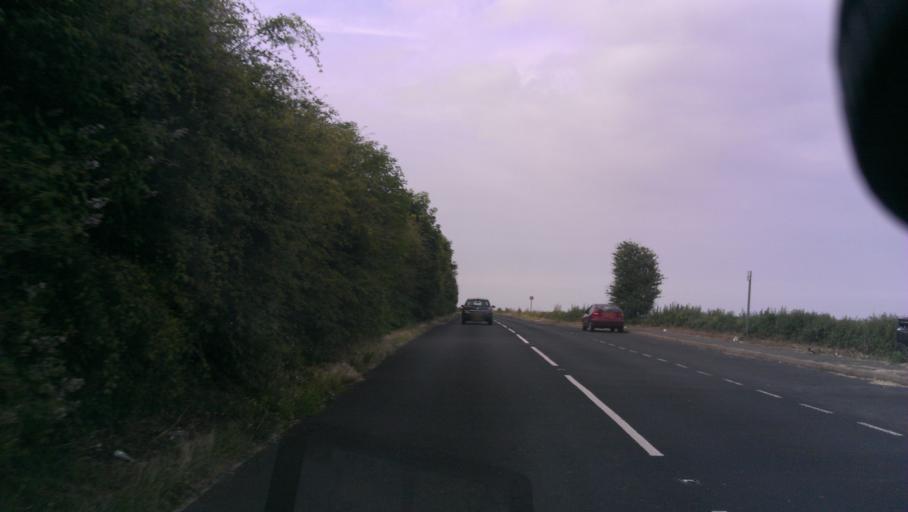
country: GB
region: England
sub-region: Kent
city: Dover
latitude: 51.1346
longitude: 1.3240
